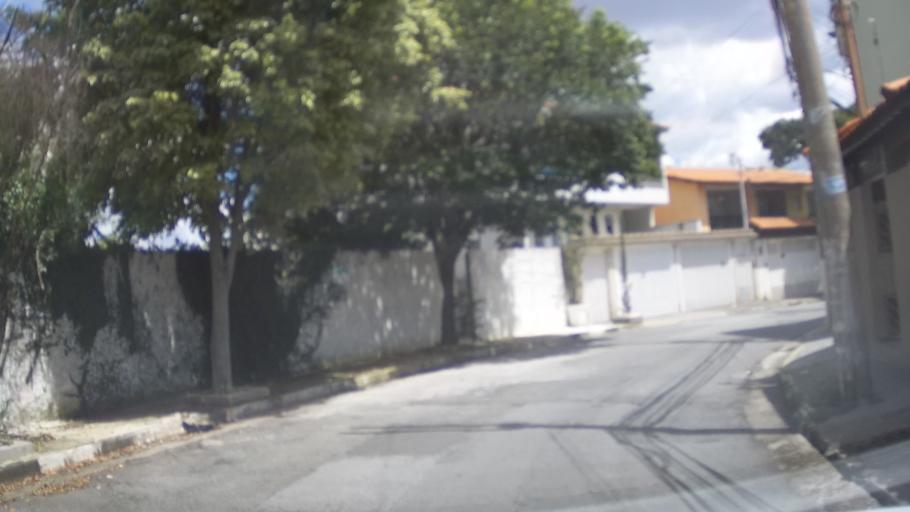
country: BR
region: Sao Paulo
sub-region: Guarulhos
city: Guarulhos
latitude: -23.4544
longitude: -46.5375
